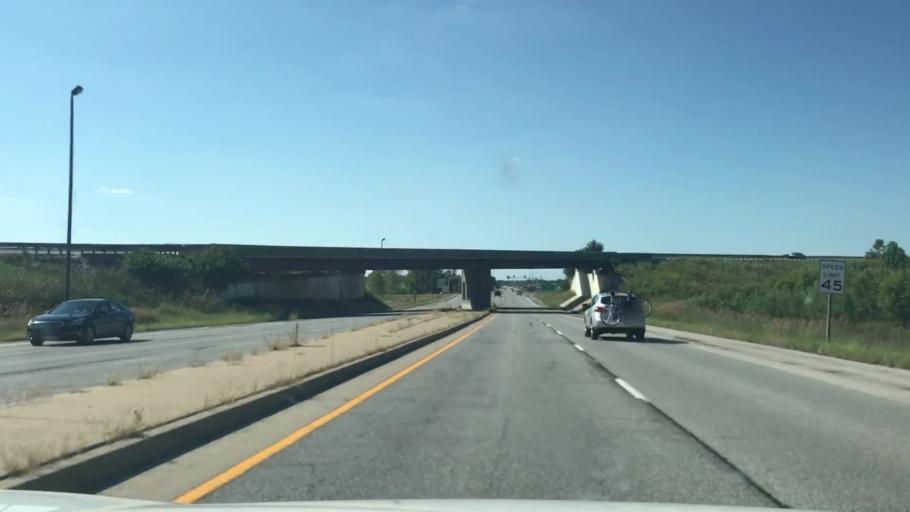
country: US
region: Illinois
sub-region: Madison County
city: South Roxana
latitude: 38.8499
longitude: -90.0504
